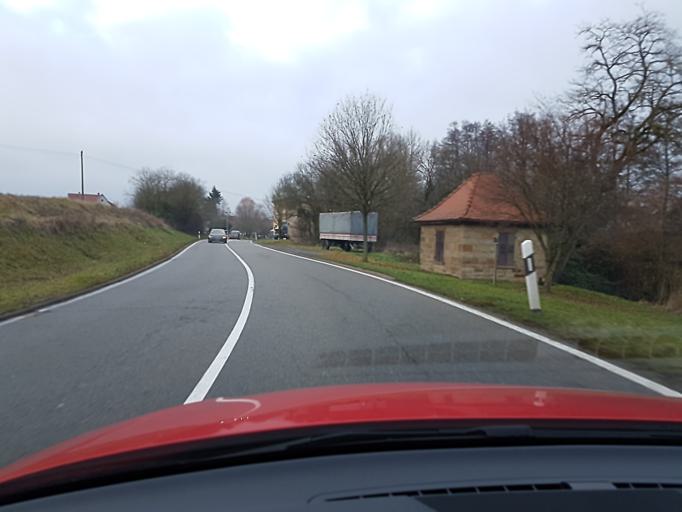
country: DE
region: Baden-Wuerttemberg
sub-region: Karlsruhe Region
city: Sternenfels
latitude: 49.0032
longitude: 8.8634
